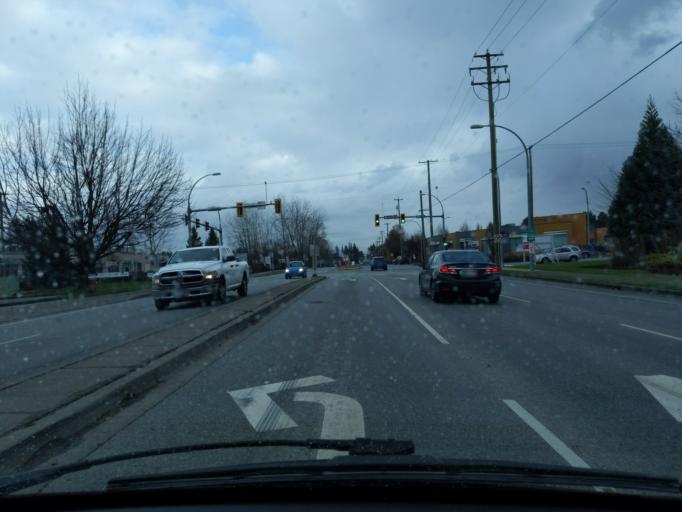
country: CA
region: British Columbia
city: Walnut Grove
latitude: 49.1769
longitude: -122.6652
